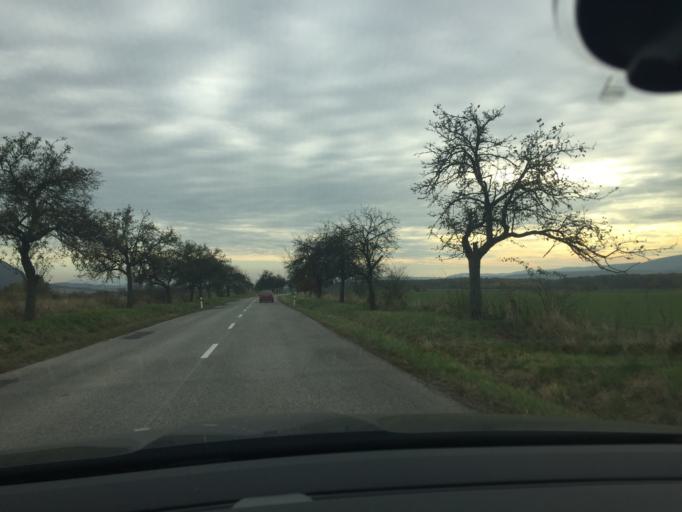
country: SK
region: Presovsky
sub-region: Okres Presov
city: Presov
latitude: 48.9291
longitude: 21.3183
